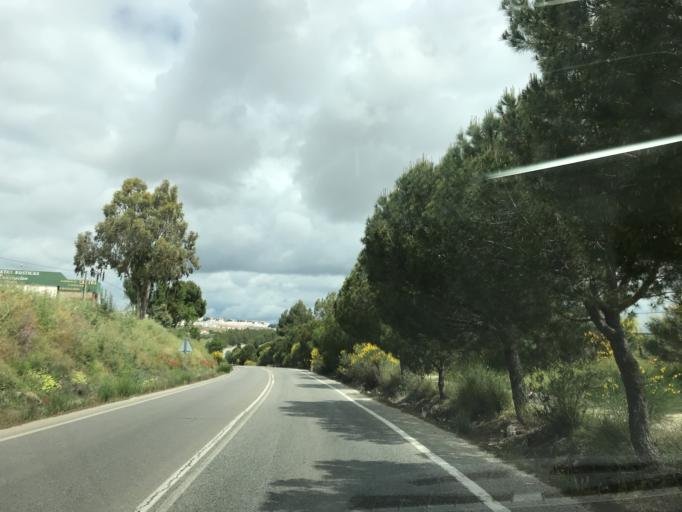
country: ES
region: Andalusia
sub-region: Provincia de Malaga
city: Ronda
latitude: 36.7333
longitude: -5.1470
